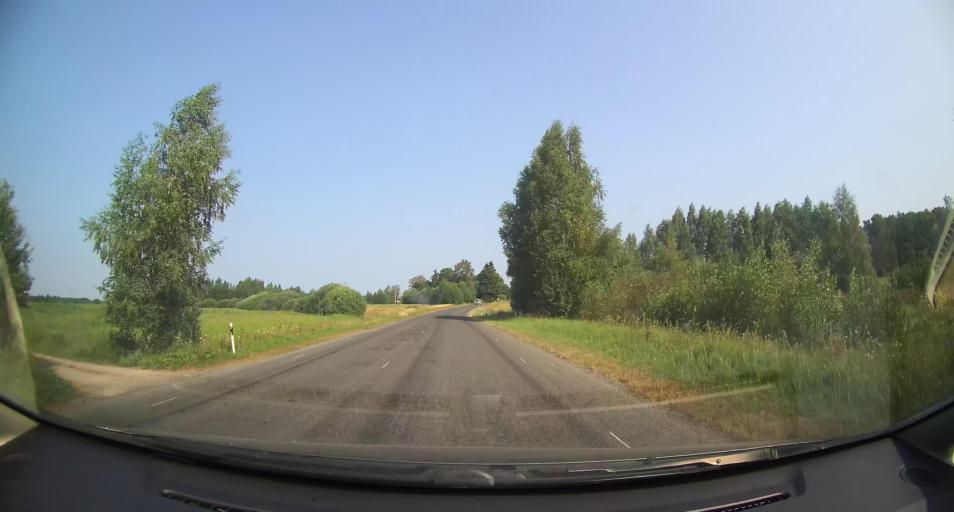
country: EE
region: Paernumaa
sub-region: Audru vald
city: Audru
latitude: 58.4390
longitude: 24.3083
